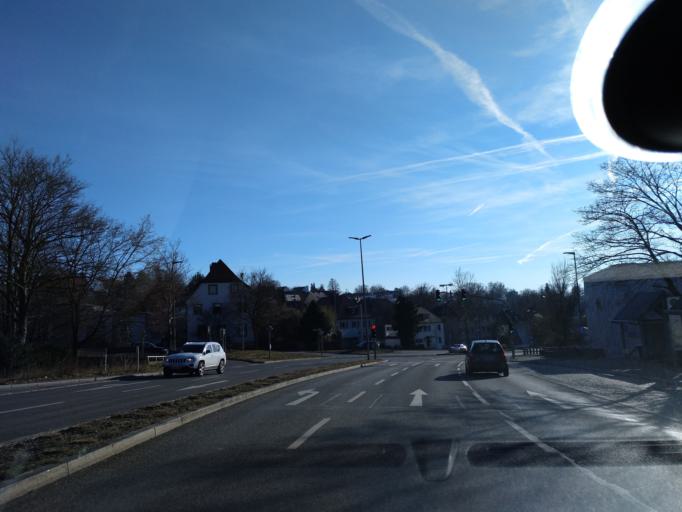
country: DE
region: Baden-Wuerttemberg
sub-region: Regierungsbezirk Stuttgart
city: Schwaebisch Hall
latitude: 49.1131
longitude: 9.7455
